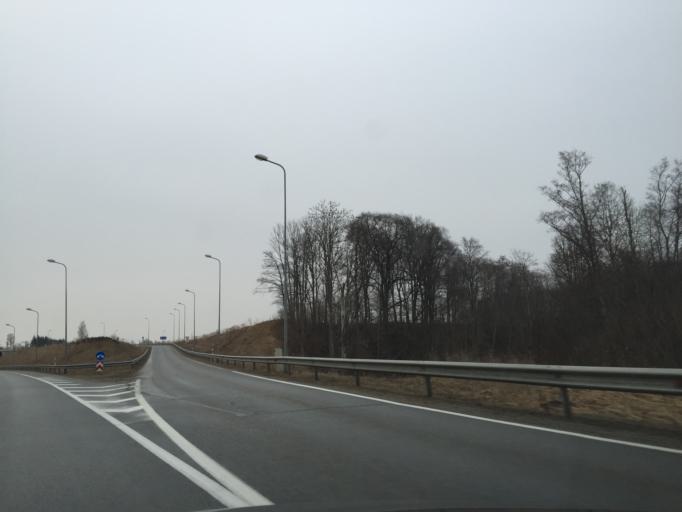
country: LV
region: Saulkrastu
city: Saulkrasti
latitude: 57.3271
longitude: 24.4559
